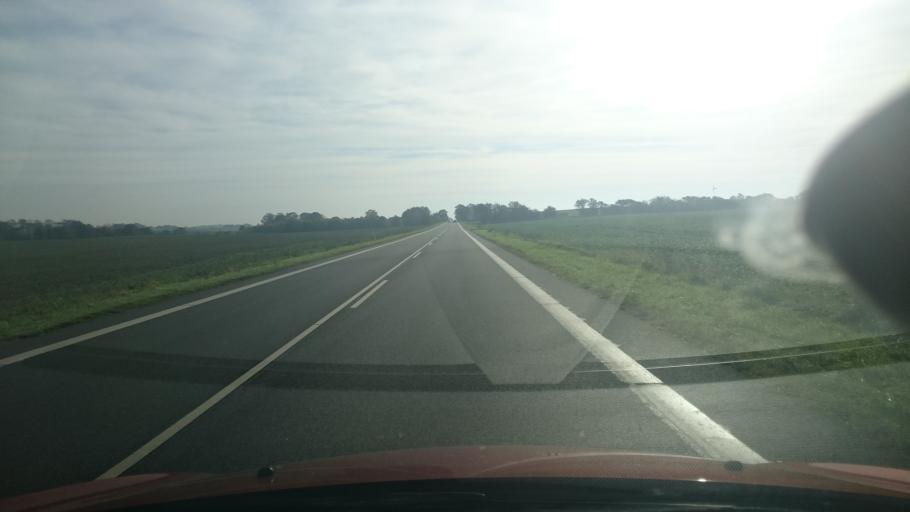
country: DK
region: Central Jutland
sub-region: Syddjurs Kommune
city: Hornslet
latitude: 56.3909
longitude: 10.2729
